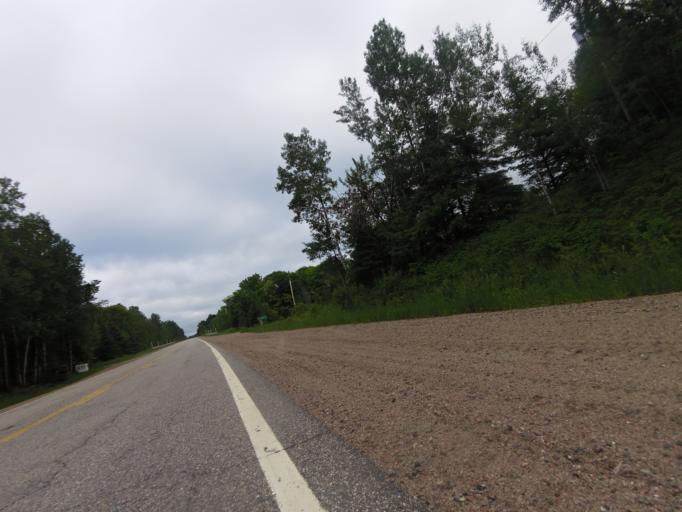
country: CA
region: Quebec
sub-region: Outaouais
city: Shawville
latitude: 45.9121
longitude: -76.3174
